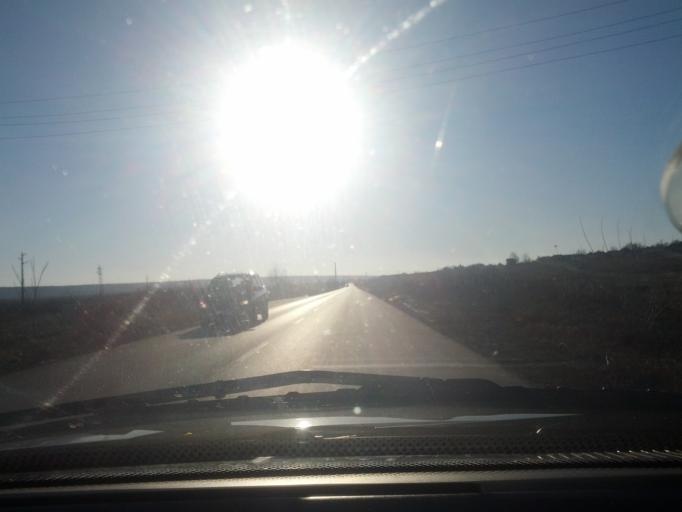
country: BG
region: Vratsa
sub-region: Obshtina Miziya
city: Miziya
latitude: 43.6615
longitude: 23.7761
